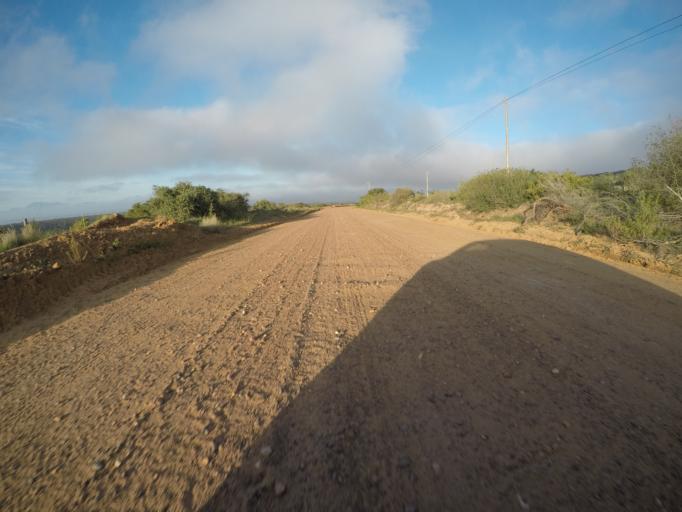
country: ZA
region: Western Cape
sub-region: Eden District Municipality
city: Mossel Bay
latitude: -34.1434
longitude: 22.0239
